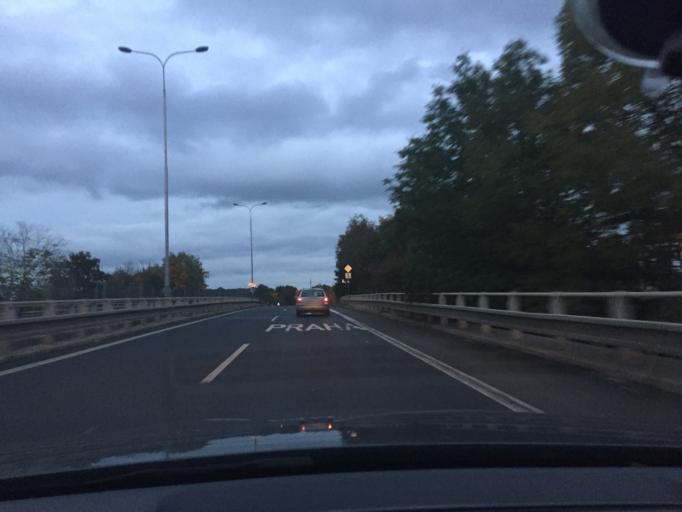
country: CZ
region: Ustecky
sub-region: Okres Teplice
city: Teplice
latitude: 50.6318
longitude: 13.8224
